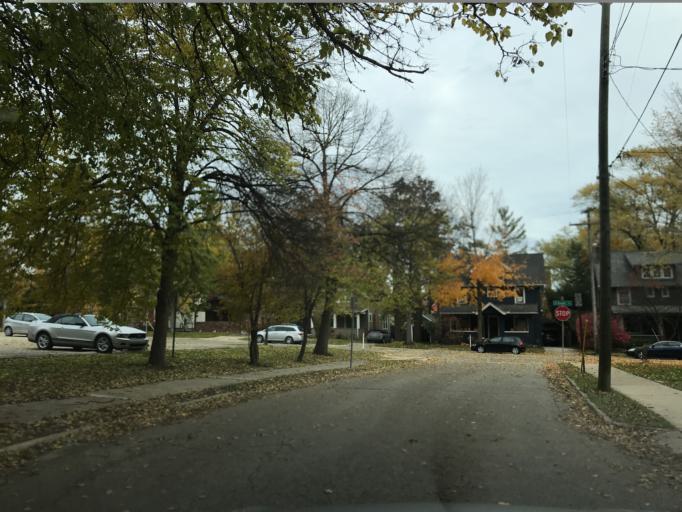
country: US
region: Michigan
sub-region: Washtenaw County
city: Ann Arbor
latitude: 42.2658
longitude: -83.7331
